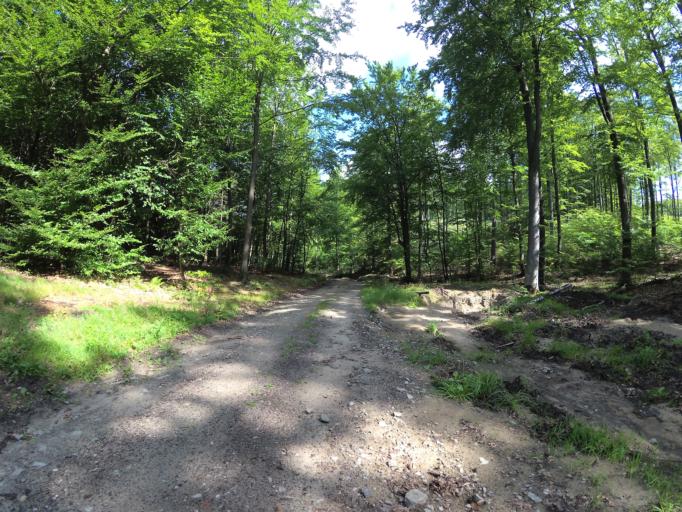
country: PL
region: Pomeranian Voivodeship
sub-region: Gdynia
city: Wielki Kack
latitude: 54.5092
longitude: 18.4549
